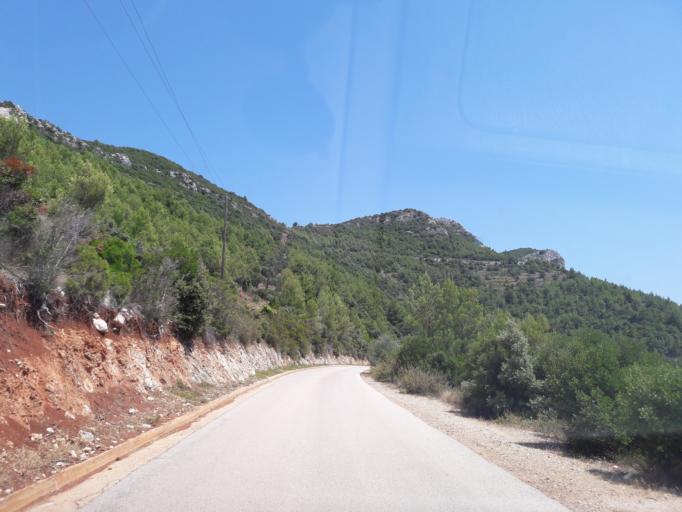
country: HR
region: Dubrovacko-Neretvanska
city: Blato
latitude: 42.9122
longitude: 17.4188
